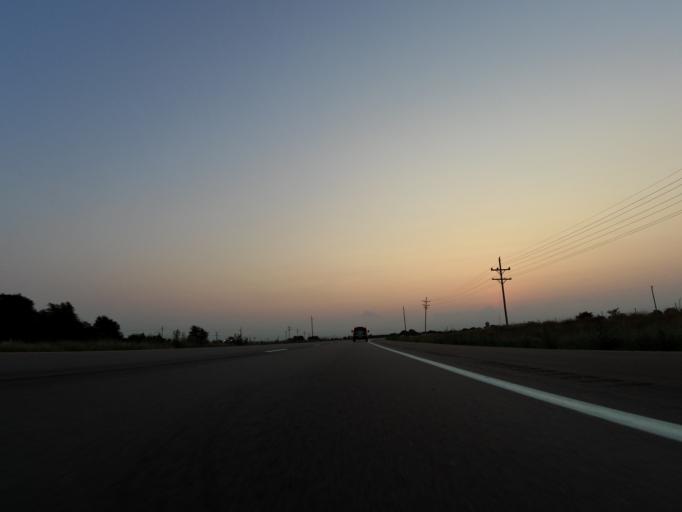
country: US
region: Kansas
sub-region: Reno County
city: South Hutchinson
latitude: 38.0114
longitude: -98.0061
